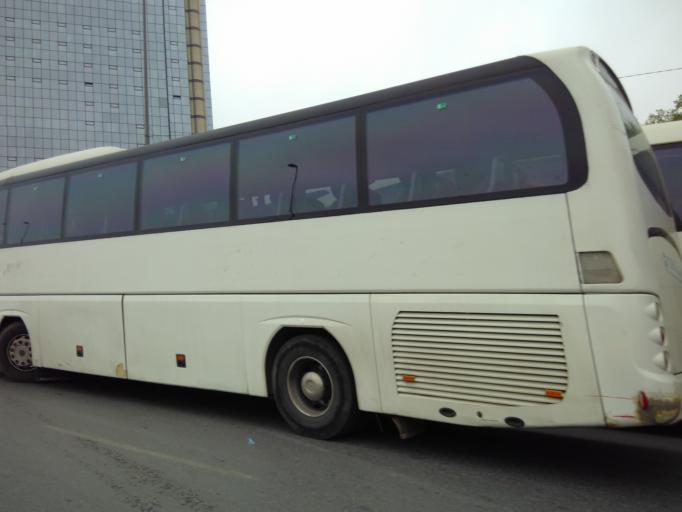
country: TR
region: Istanbul
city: Sisli
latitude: 41.0412
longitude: 28.9930
